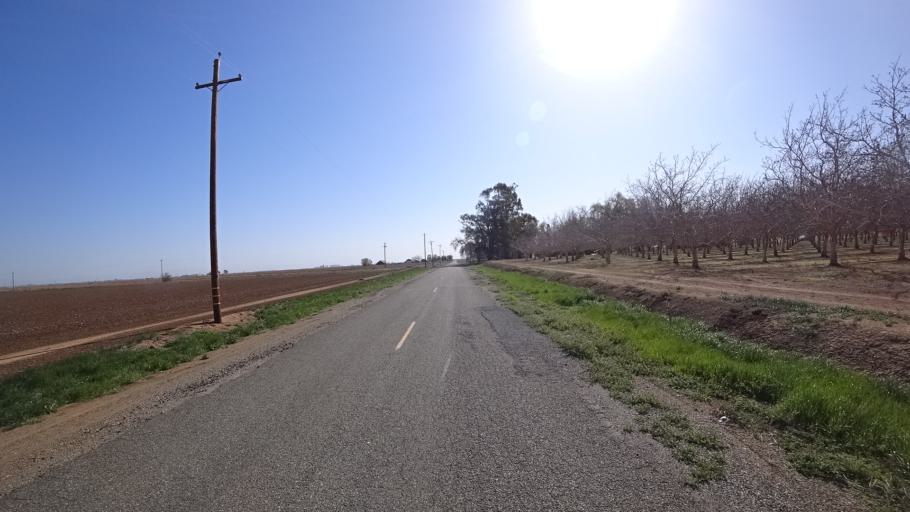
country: US
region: California
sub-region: Glenn County
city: Willows
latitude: 39.4522
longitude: -122.2413
